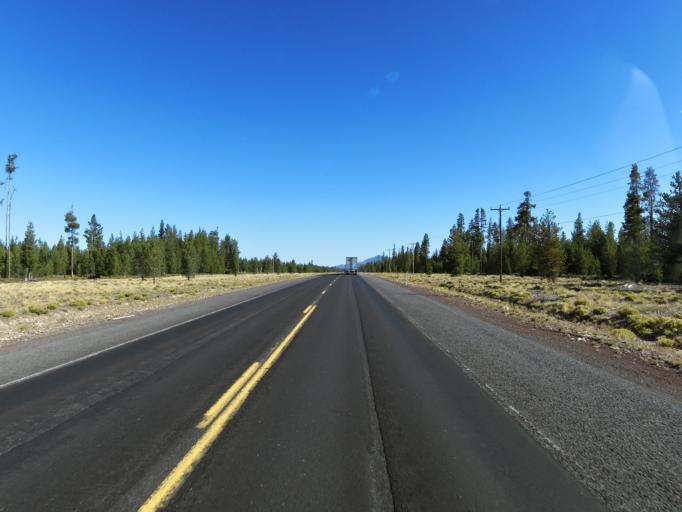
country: US
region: Oregon
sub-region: Deschutes County
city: La Pine
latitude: 43.1440
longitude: -121.7989
